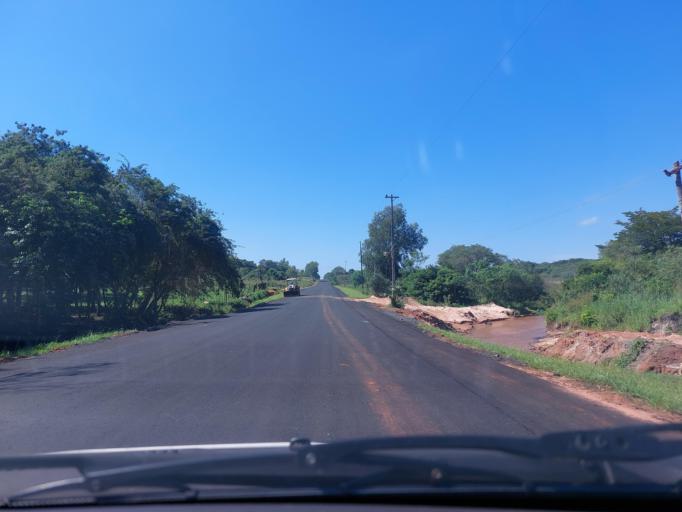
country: PY
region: San Pedro
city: Guayaybi
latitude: -24.5502
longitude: -56.5121
